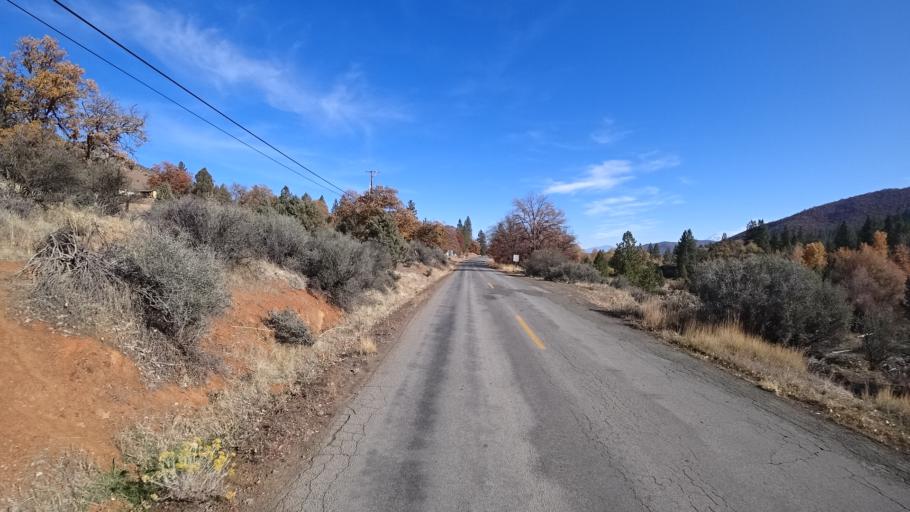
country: US
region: California
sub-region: Siskiyou County
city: Yreka
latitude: 41.7176
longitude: -122.6705
